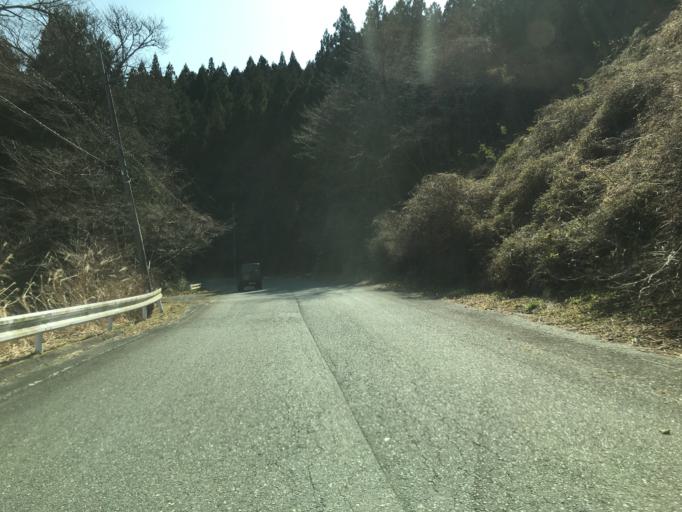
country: JP
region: Ibaraki
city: Takahagi
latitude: 36.8172
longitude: 140.5777
